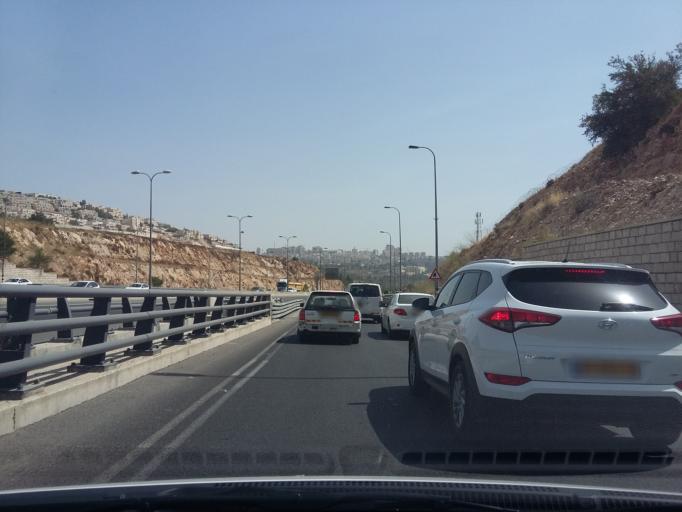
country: PS
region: West Bank
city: Bir Nabala
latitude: 31.8225
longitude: 35.2141
